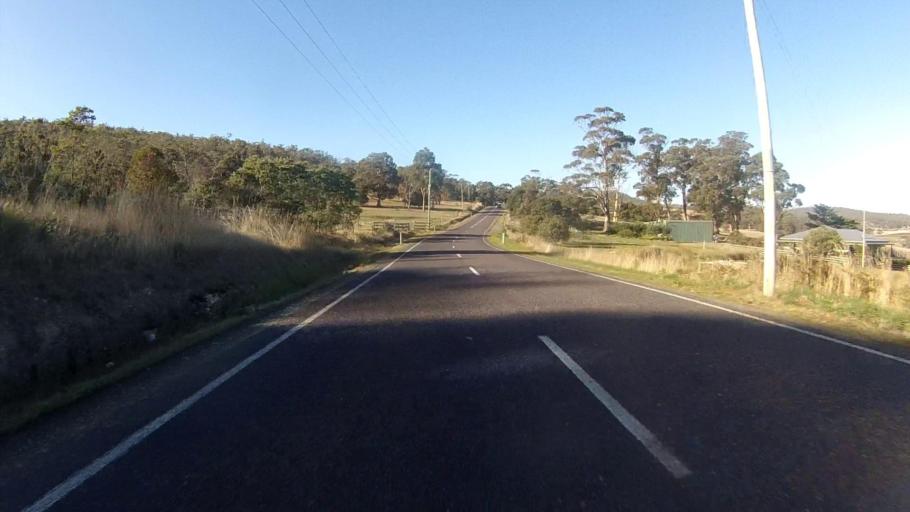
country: AU
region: Tasmania
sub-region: Sorell
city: Sorell
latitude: -42.8113
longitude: 147.6520
